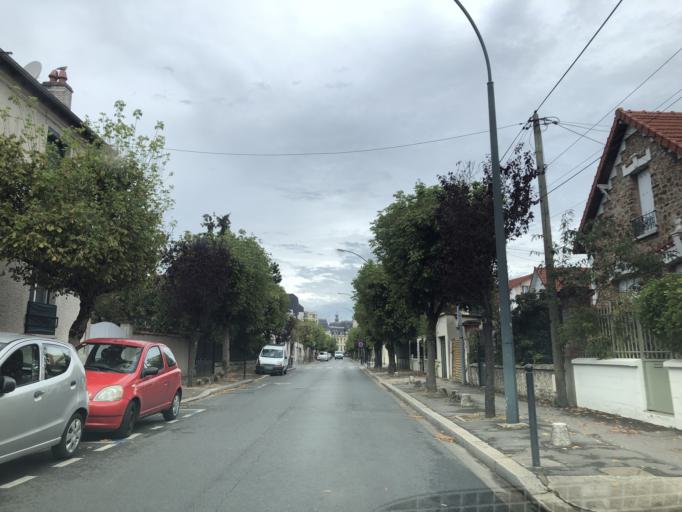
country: FR
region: Ile-de-France
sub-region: Departement du Val-de-Marne
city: Saint-Maur-des-Fosses
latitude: 48.7998
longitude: 2.4892
